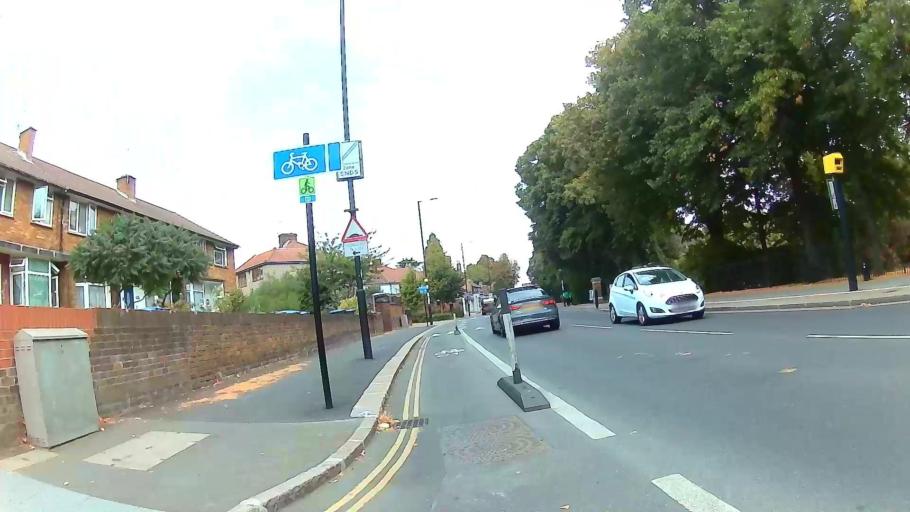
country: GB
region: England
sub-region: Greater London
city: Enfield
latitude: 51.6545
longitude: -0.0485
